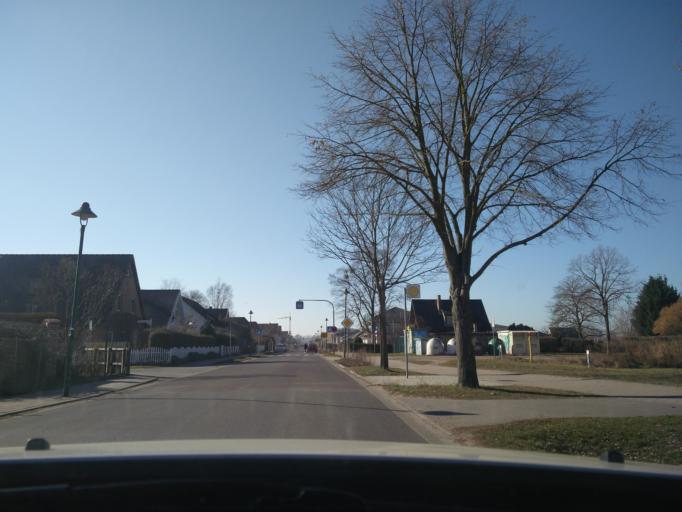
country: DE
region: Brandenburg
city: Brieselang
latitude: 52.5806
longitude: 12.9847
